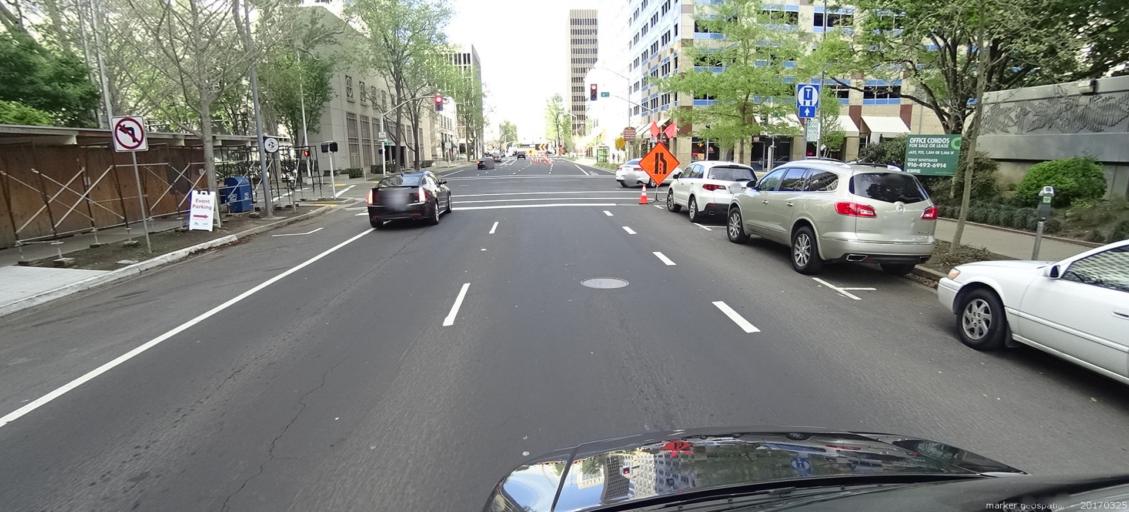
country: US
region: California
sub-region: Sacramento County
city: Sacramento
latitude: 38.5774
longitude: -121.5022
